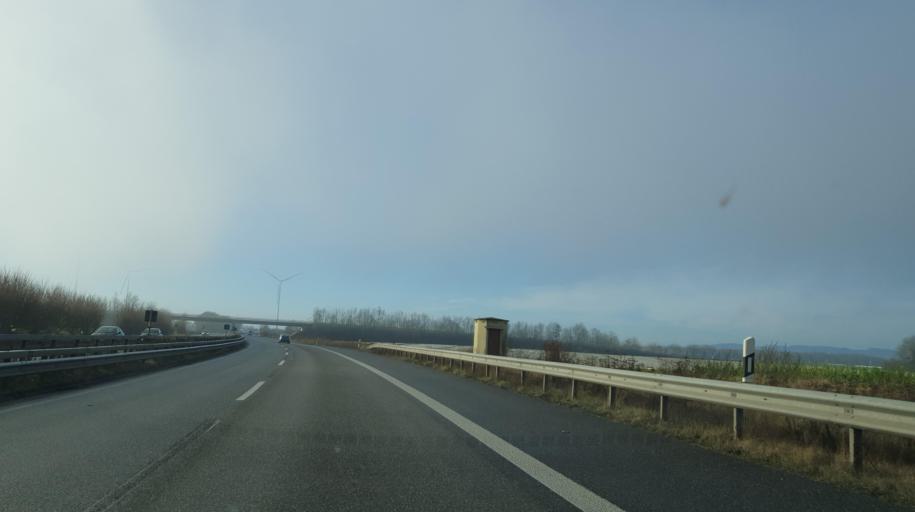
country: DE
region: Rheinland-Pfalz
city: Harthausen
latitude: 49.2893
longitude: 8.3717
